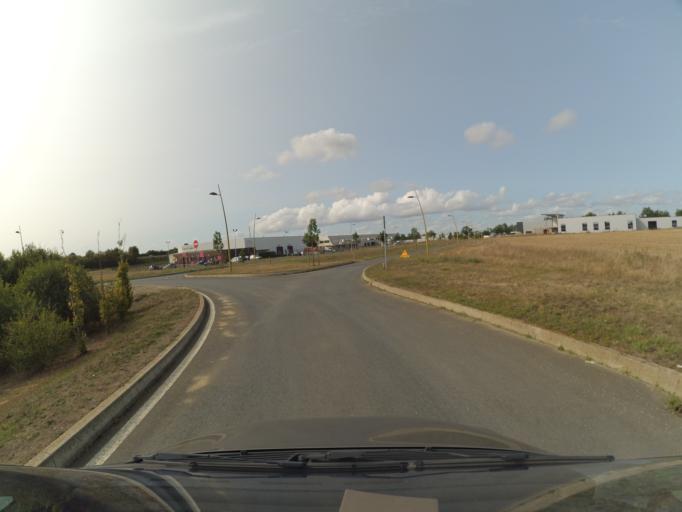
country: FR
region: Pays de la Loire
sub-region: Departement de la Vendee
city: Bouffere
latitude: 46.9479
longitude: -1.3446
